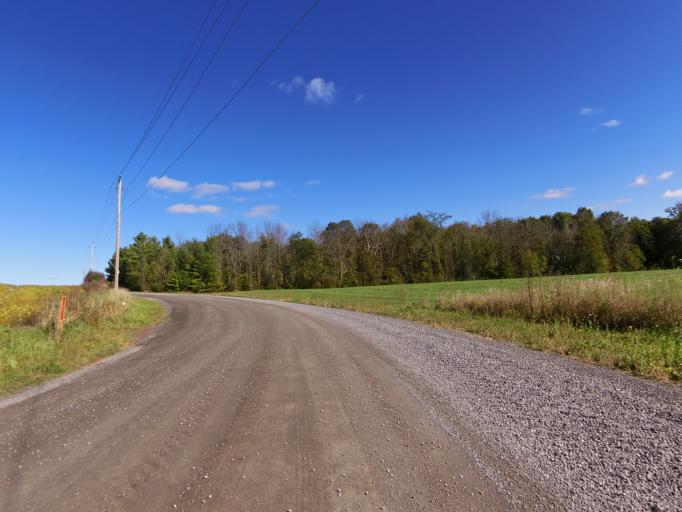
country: CA
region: Ontario
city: Clarence-Rockland
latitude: 45.4102
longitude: -75.3721
